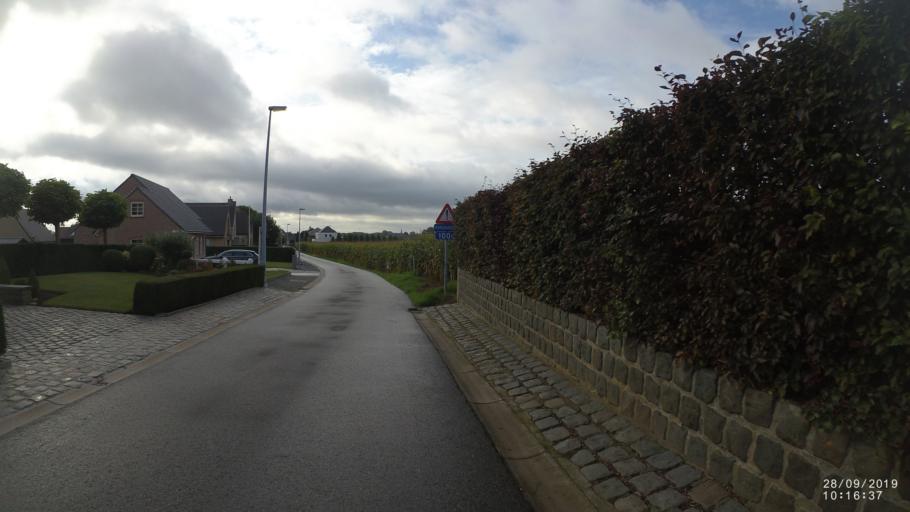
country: BE
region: Flanders
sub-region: Provincie Oost-Vlaanderen
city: Sint-Maria-Lierde
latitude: 50.8139
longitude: 3.8213
